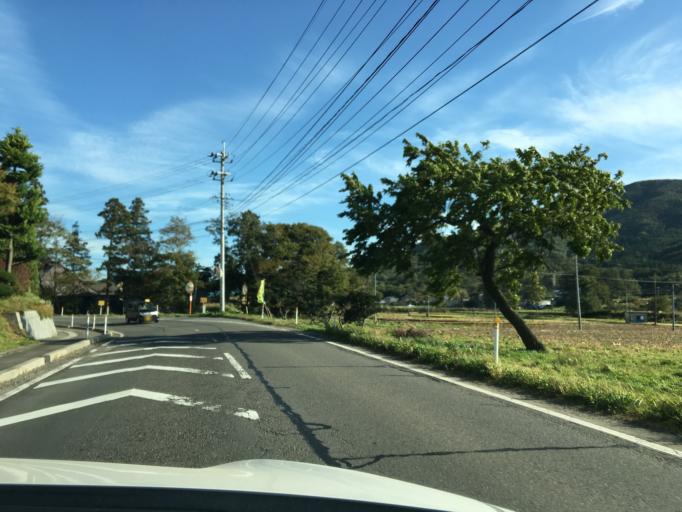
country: JP
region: Fukushima
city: Funehikimachi-funehiki
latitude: 37.3385
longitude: 140.5696
